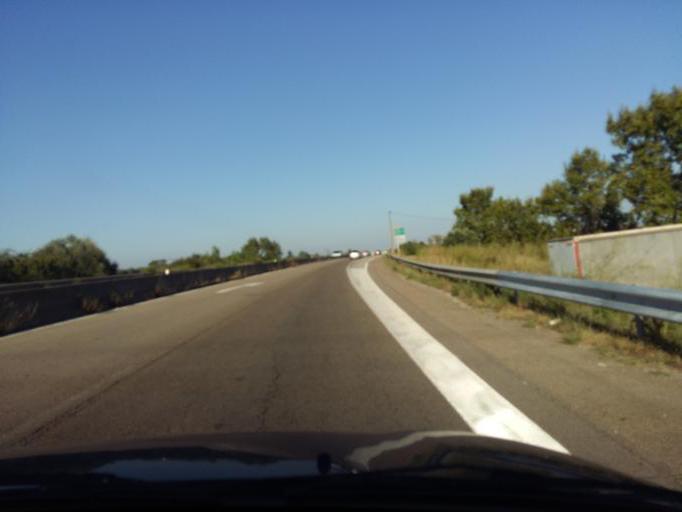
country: FR
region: Languedoc-Roussillon
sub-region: Departement du Gard
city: Marguerittes
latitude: 43.8609
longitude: 4.4288
